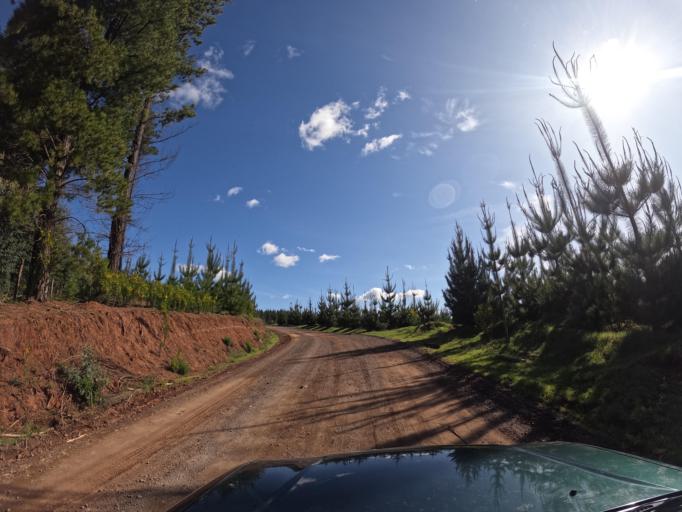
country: CL
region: Biobio
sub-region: Provincia de Biobio
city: La Laja
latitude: -37.0893
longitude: -72.8287
